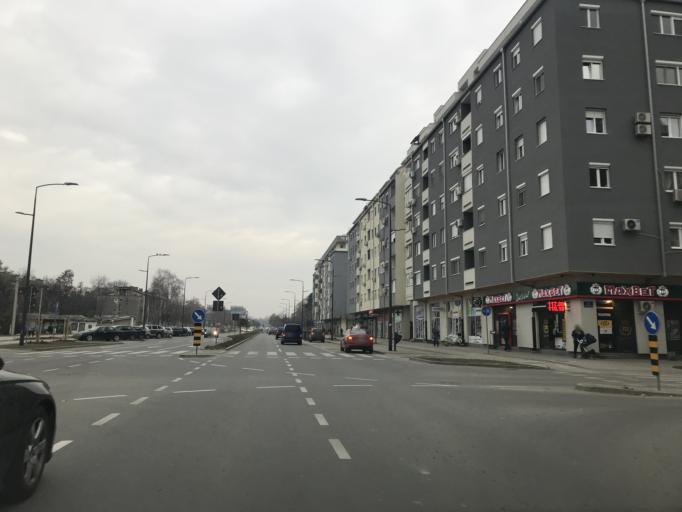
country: RS
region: Autonomna Pokrajina Vojvodina
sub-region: Juznobacki Okrug
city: Novi Sad
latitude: 45.2479
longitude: 19.7994
